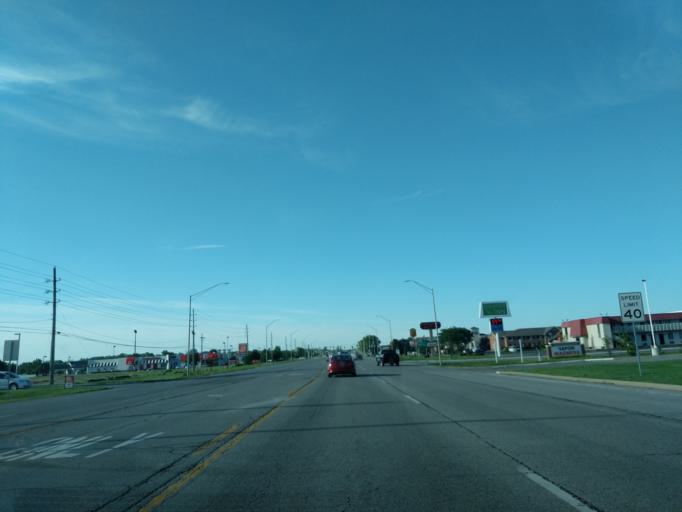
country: US
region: Indiana
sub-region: Hancock County
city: Greenfield
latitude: 39.8179
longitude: -85.7700
